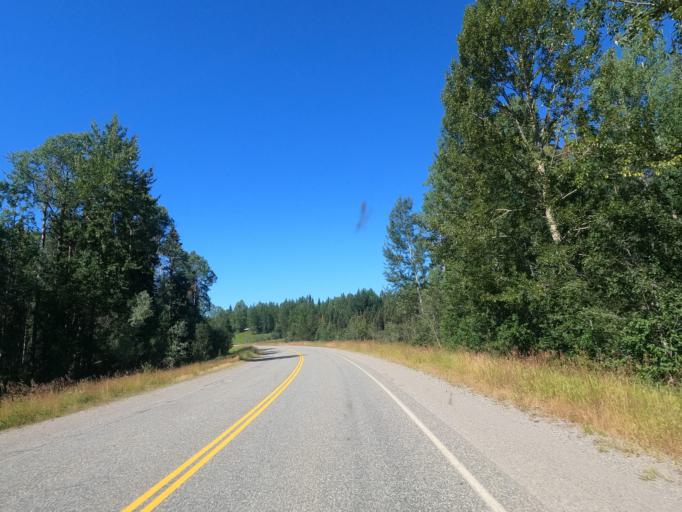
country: CA
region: British Columbia
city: Quesnel
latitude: 53.0557
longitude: -122.1709
